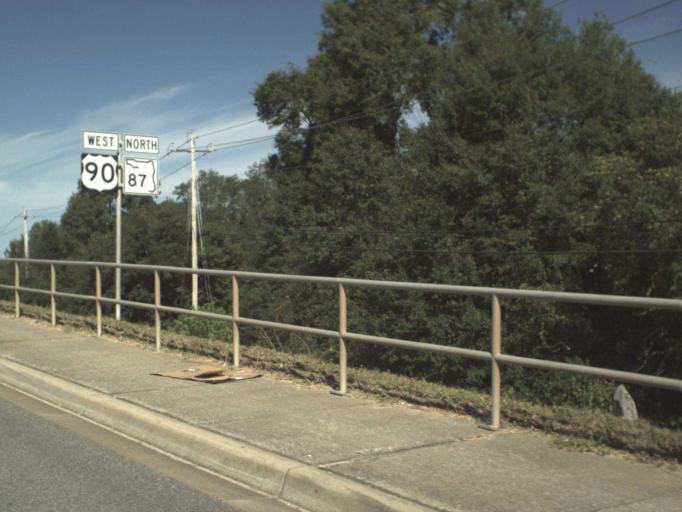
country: US
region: Florida
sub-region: Santa Rosa County
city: East Milton
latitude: 30.6252
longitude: -87.0221
